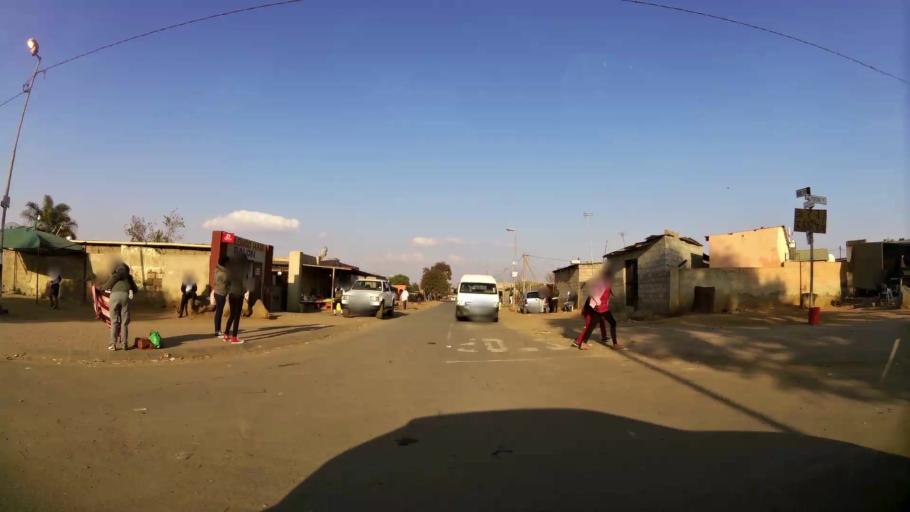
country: ZA
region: Gauteng
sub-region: Ekurhuleni Metropolitan Municipality
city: Tembisa
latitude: -25.9840
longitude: 28.2038
